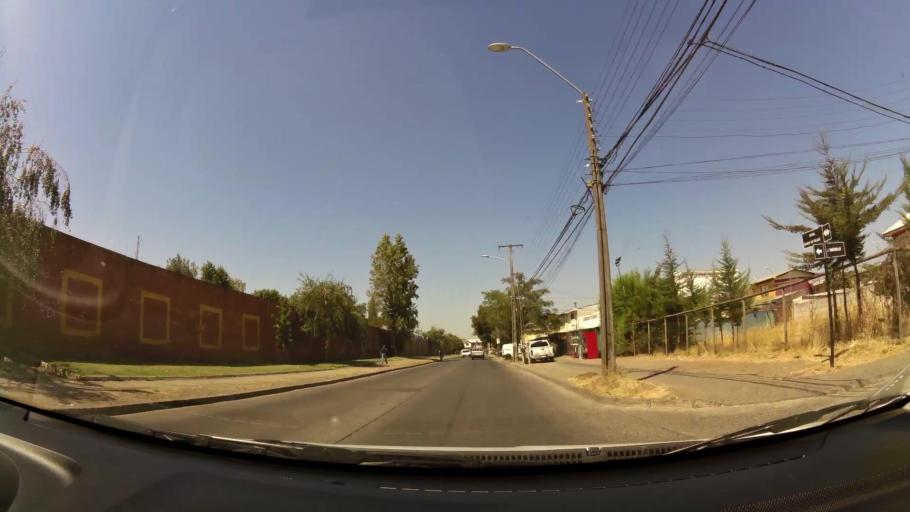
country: CL
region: Maule
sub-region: Provincia de Curico
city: Curico
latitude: -34.9751
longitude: -71.2353
